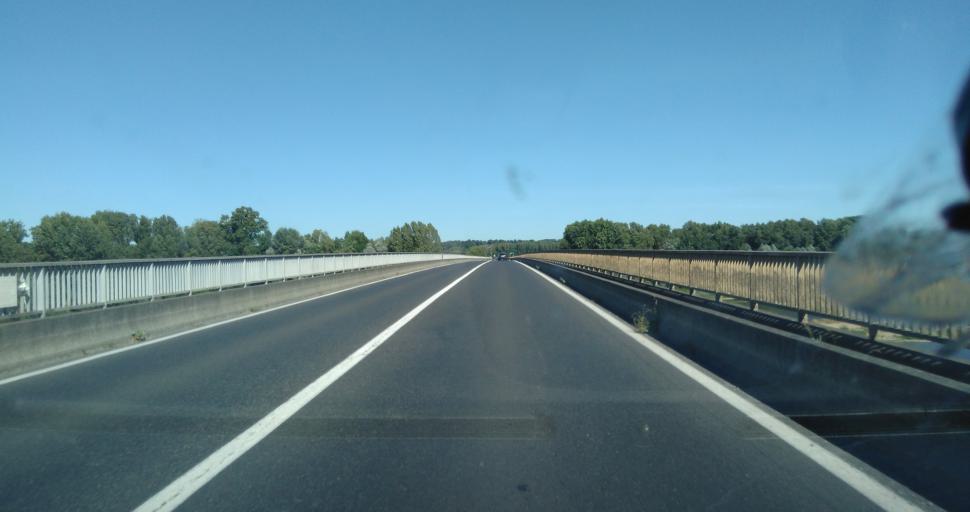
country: FR
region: Centre
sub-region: Departement d'Indre-et-Loire
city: Charge
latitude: 47.4272
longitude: 1.0102
